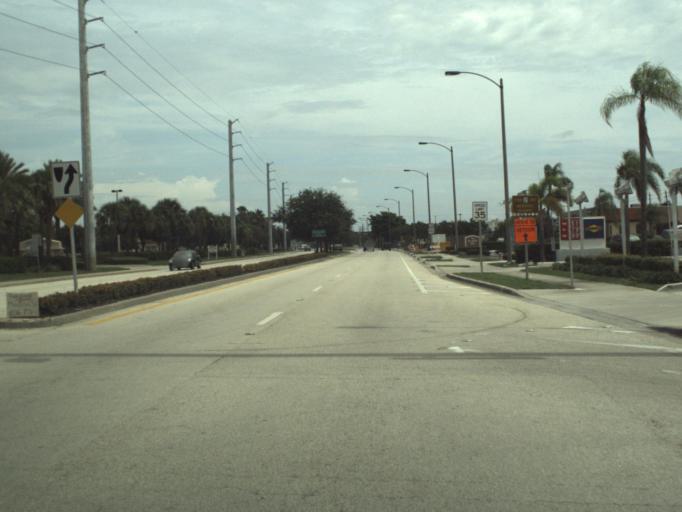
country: US
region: Florida
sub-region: Palm Beach County
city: Lake Park
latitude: 26.8037
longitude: -80.0552
